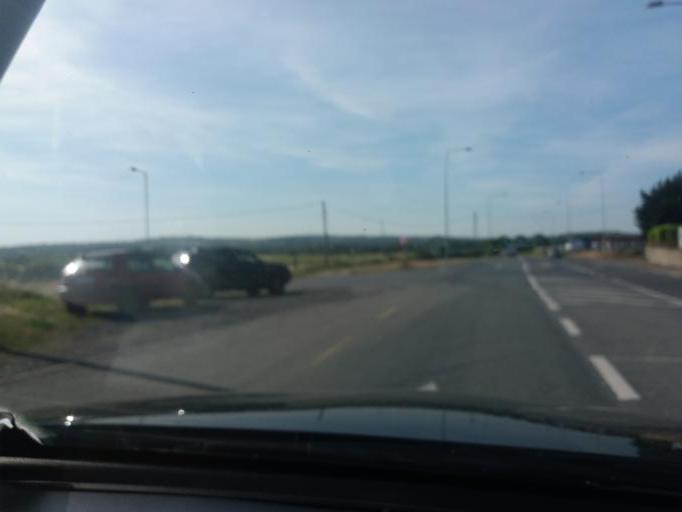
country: IE
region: Leinster
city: Lusk
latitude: 53.5328
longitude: -6.1950
